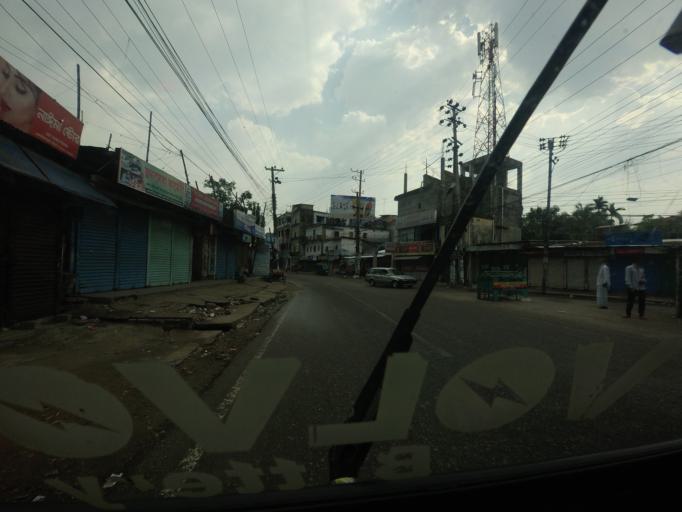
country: BD
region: Sylhet
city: Sylhet
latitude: 24.9136
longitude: 91.8728
